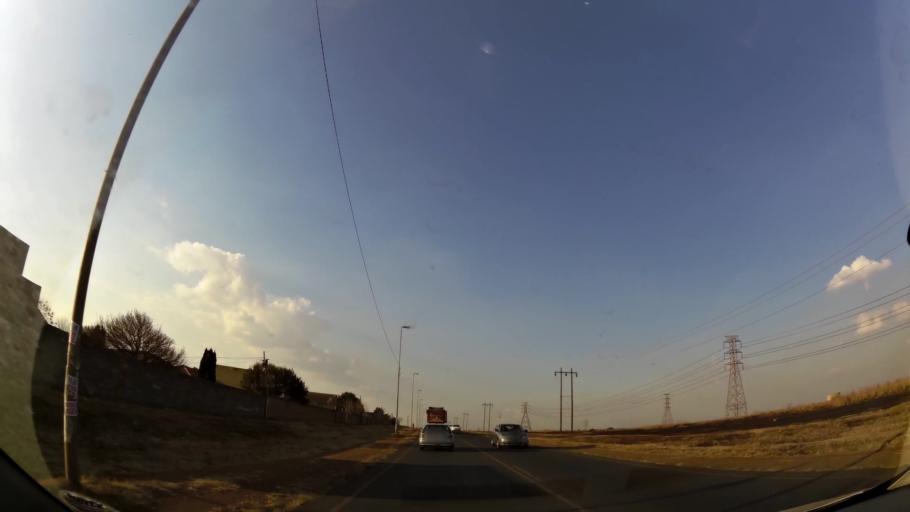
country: ZA
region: Gauteng
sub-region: Ekurhuleni Metropolitan Municipality
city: Boksburg
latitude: -26.3120
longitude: 28.2566
